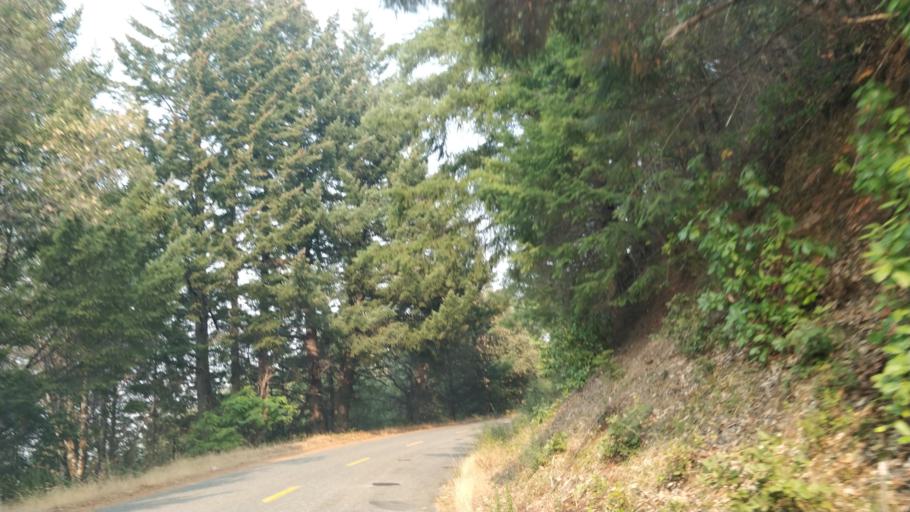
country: US
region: California
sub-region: Humboldt County
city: Rio Dell
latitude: 40.2628
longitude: -124.1131
